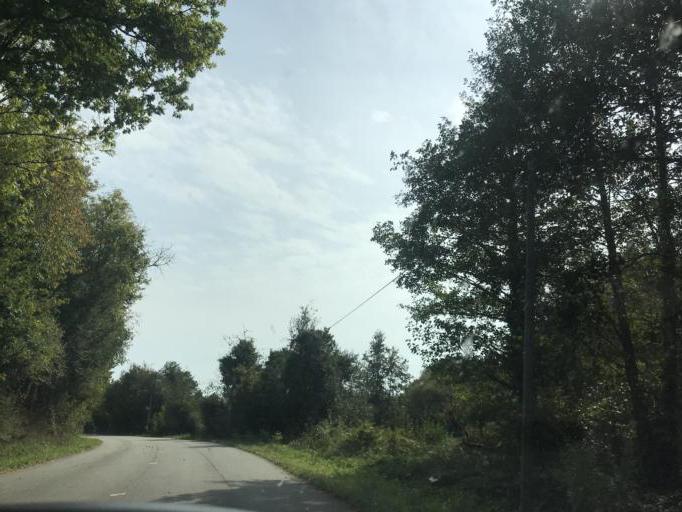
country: FR
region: Brittany
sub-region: Departement du Finistere
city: Loperec
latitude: 48.2969
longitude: -4.0177
